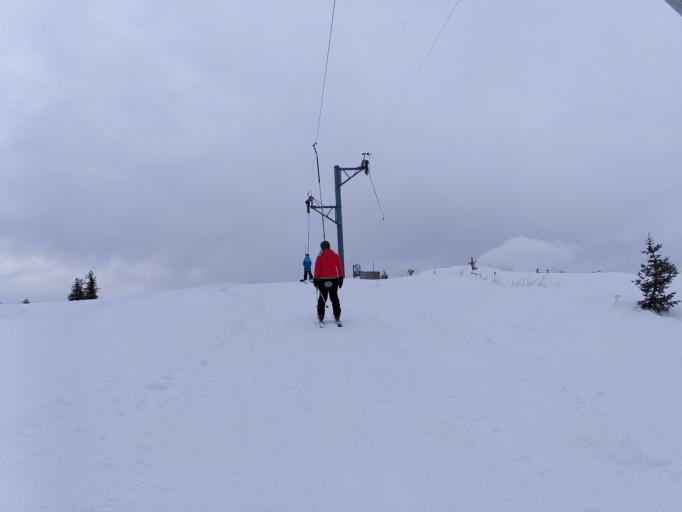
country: NO
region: Buskerud
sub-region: Flesberg
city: Lampeland
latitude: 59.8006
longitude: 9.3894
